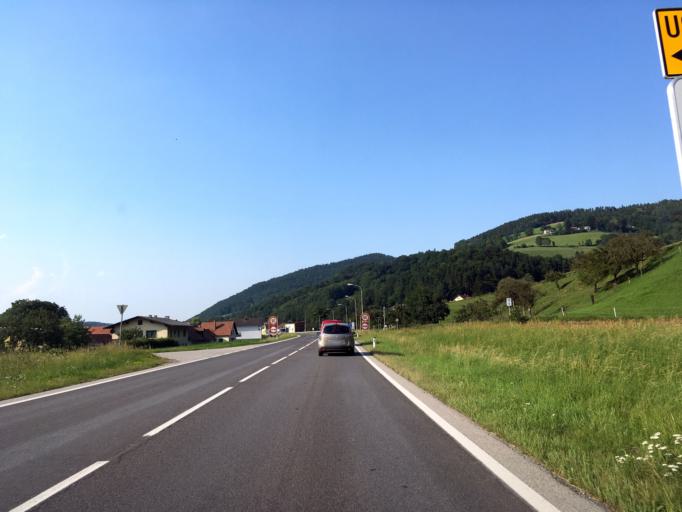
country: AT
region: Lower Austria
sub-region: Politischer Bezirk Neunkirchen
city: Grimmenstein
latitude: 47.6301
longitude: 16.1321
